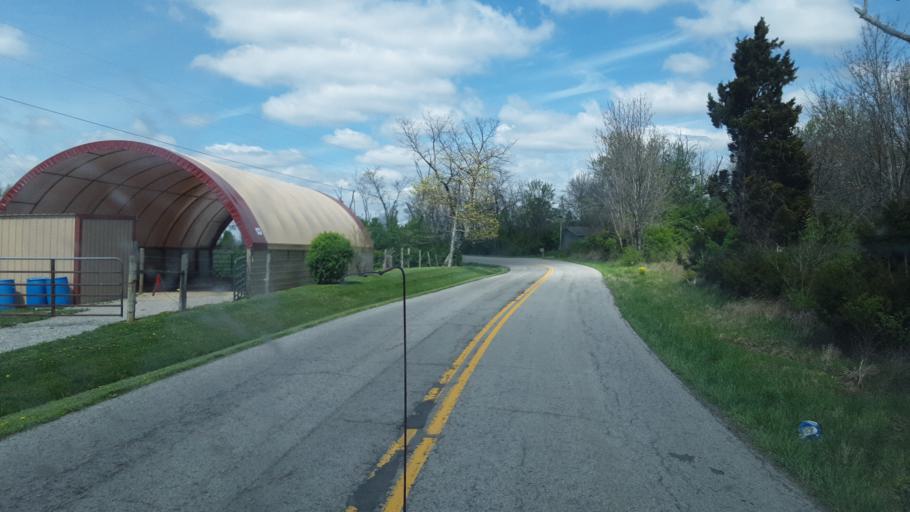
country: US
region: Kentucky
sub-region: Grant County
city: Dry Ridge
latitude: 38.6604
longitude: -84.6955
